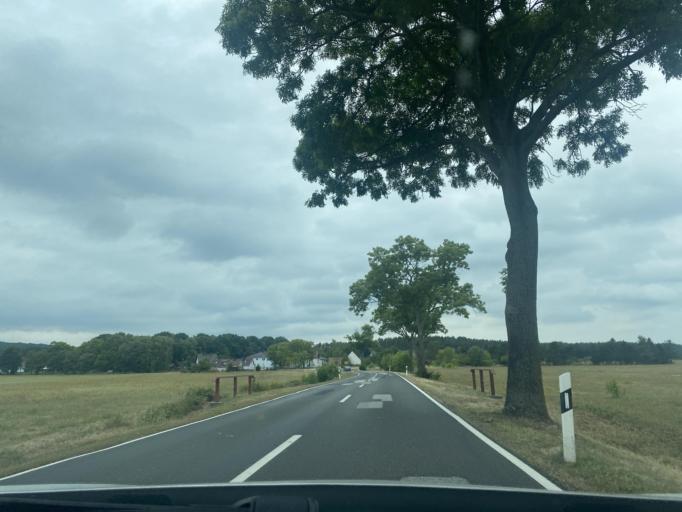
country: DE
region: Saxony
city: Mucka
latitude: 51.2825
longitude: 14.7000
